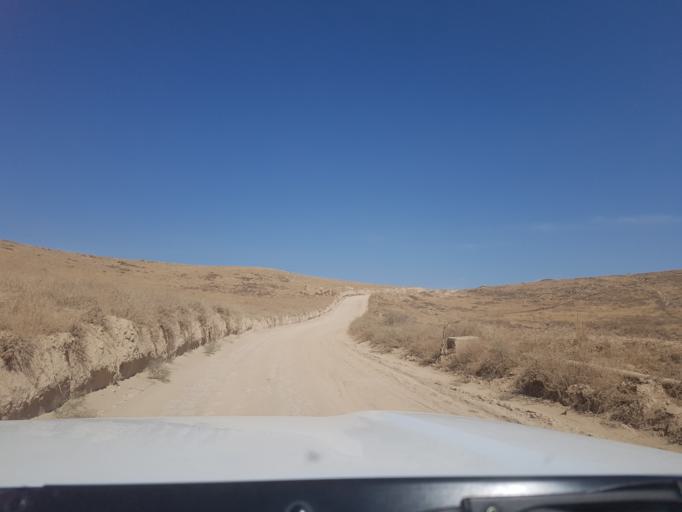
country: TM
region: Ahal
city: Baharly
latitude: 38.2660
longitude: 56.8870
